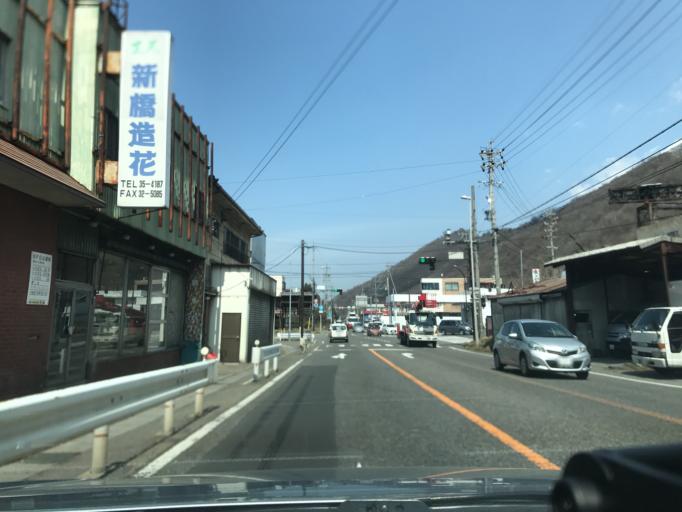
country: JP
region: Nagano
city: Matsumoto
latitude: 36.2474
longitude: 137.9521
